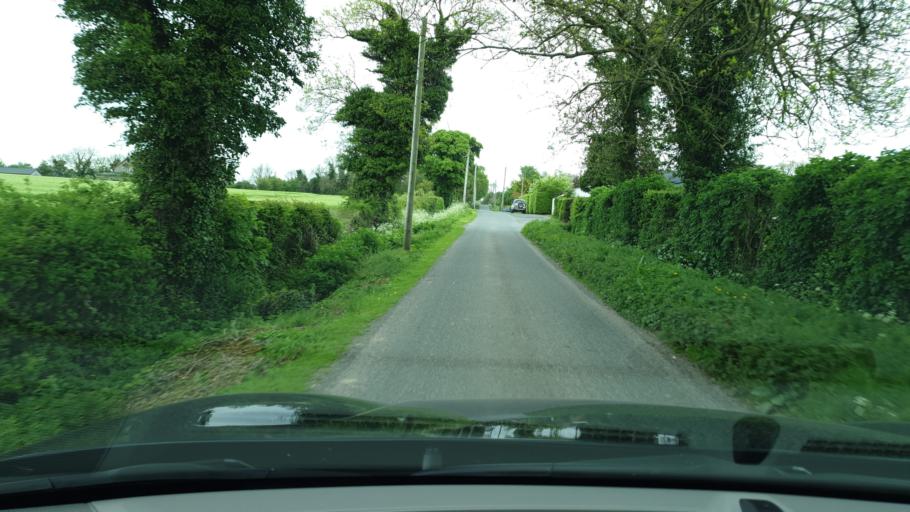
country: IE
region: Leinster
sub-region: An Mhi
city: Ratoath
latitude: 53.4948
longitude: -6.4920
